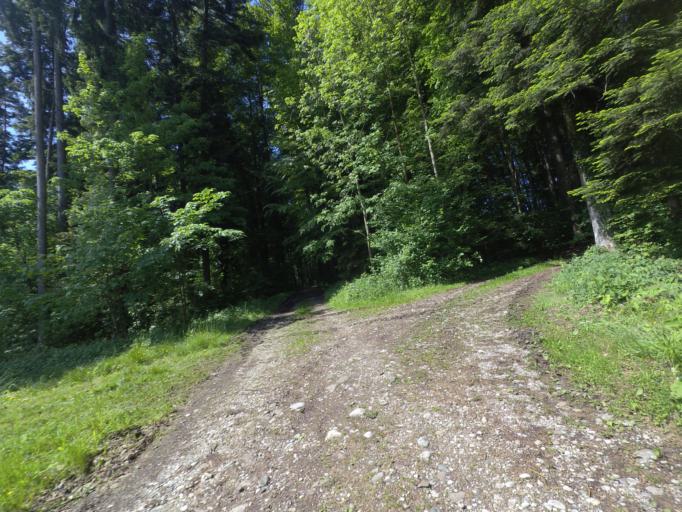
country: DE
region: Bavaria
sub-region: Upper Bavaria
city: Petting
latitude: 47.8987
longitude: 12.8062
